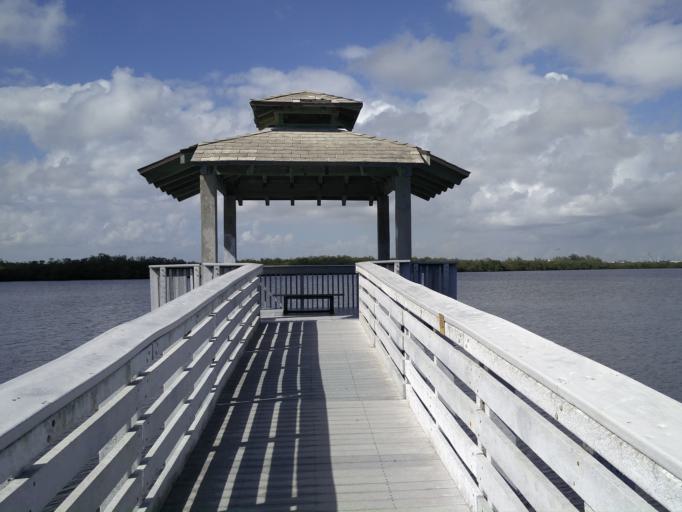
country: US
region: Florida
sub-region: Broward County
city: Dania Beach
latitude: 26.0398
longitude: -80.1225
